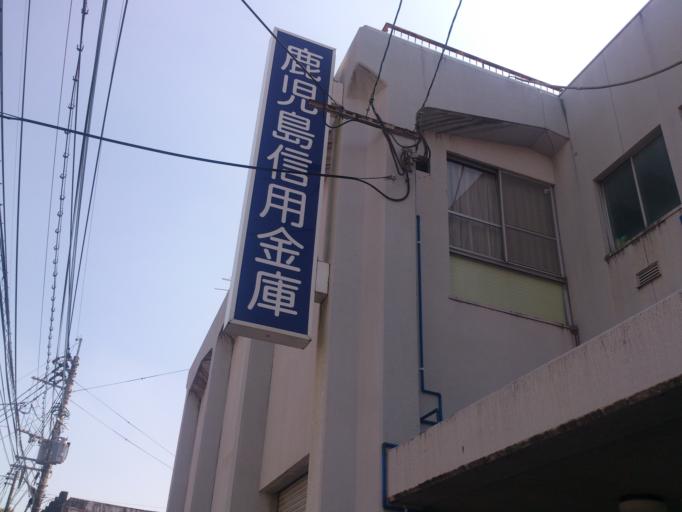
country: JP
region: Kagoshima
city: Kanoya
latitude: 31.3863
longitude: 130.8501
